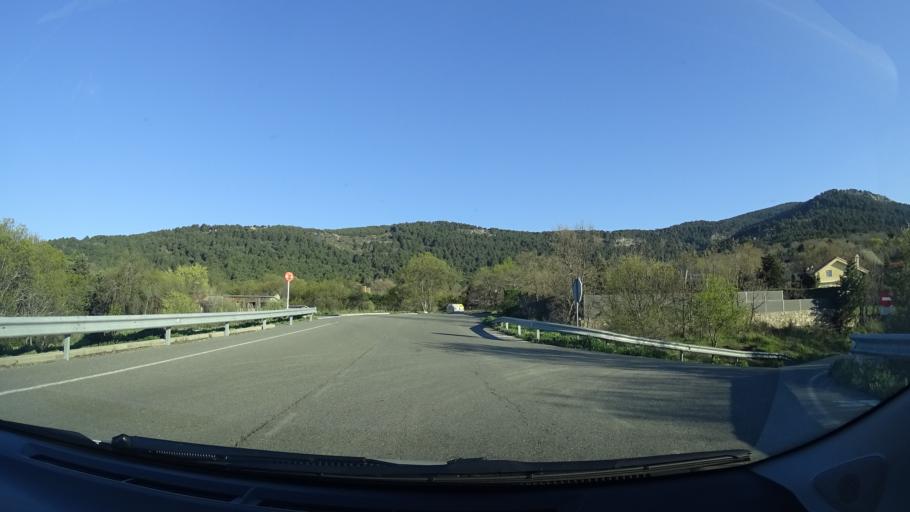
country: ES
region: Madrid
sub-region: Provincia de Madrid
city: Navacerrada
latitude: 40.7363
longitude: -4.0064
